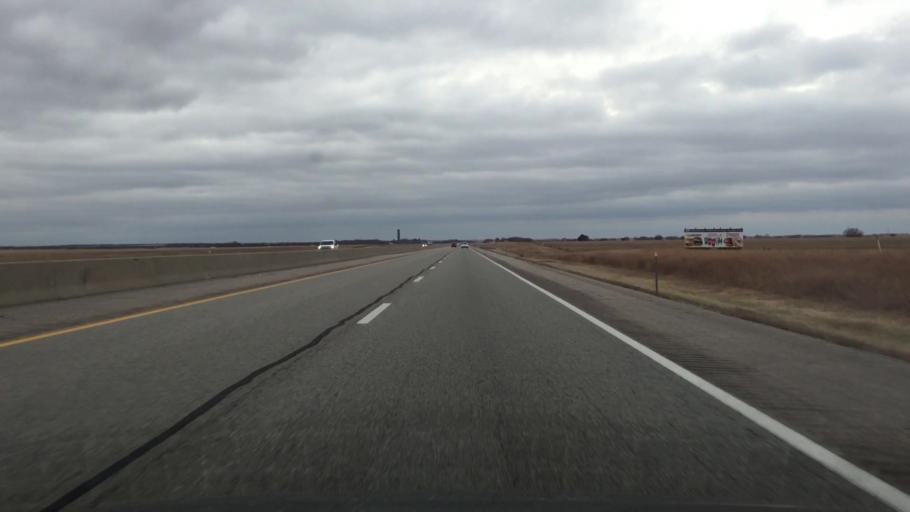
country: US
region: Kansas
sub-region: Butler County
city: El Dorado
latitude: 37.9062
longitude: -96.8209
